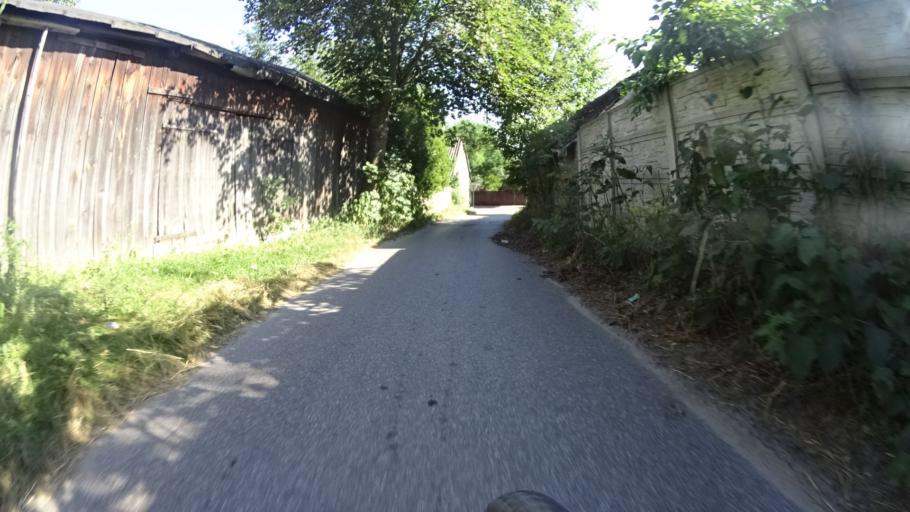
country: PL
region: Masovian Voivodeship
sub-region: Powiat bialobrzeski
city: Wysmierzyce
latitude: 51.6632
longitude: 20.8637
